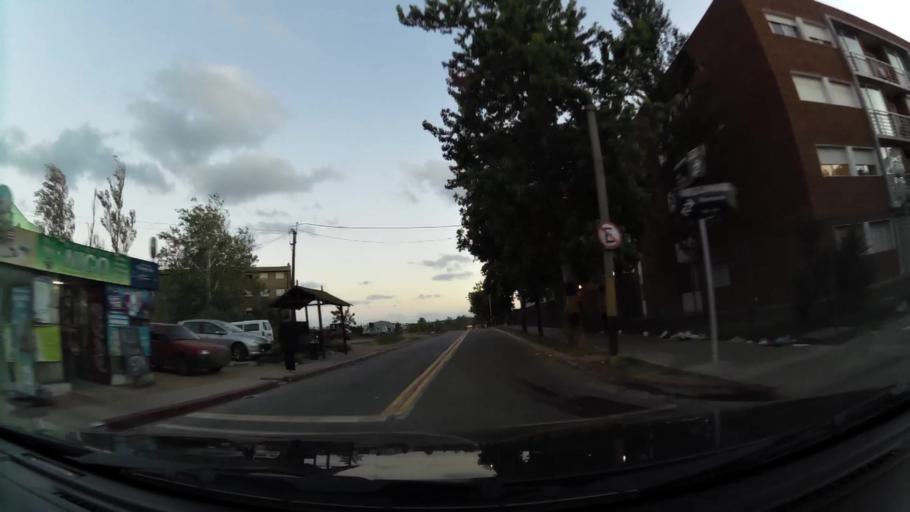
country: UY
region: Canelones
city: Paso de Carrasco
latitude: -34.8746
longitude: -56.1039
